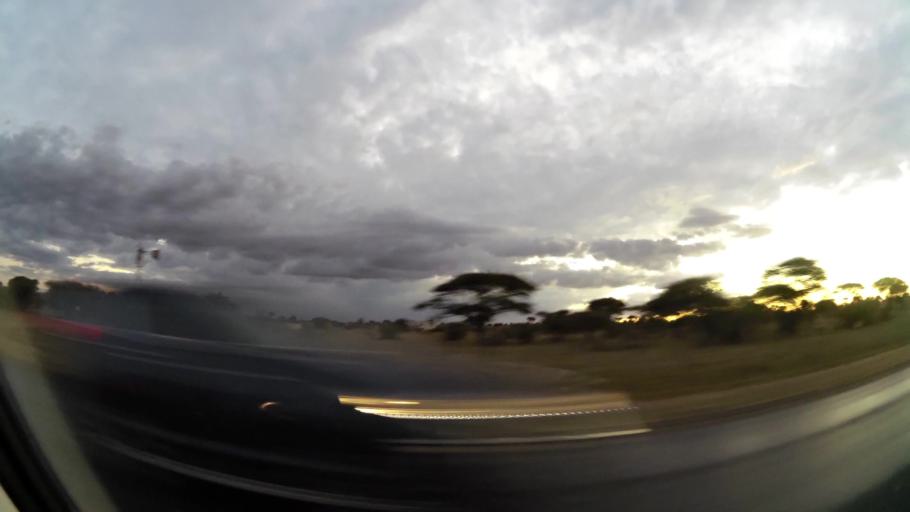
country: ZA
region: Limpopo
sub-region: Capricorn District Municipality
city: Polokwane
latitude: -23.8398
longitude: 29.4272
